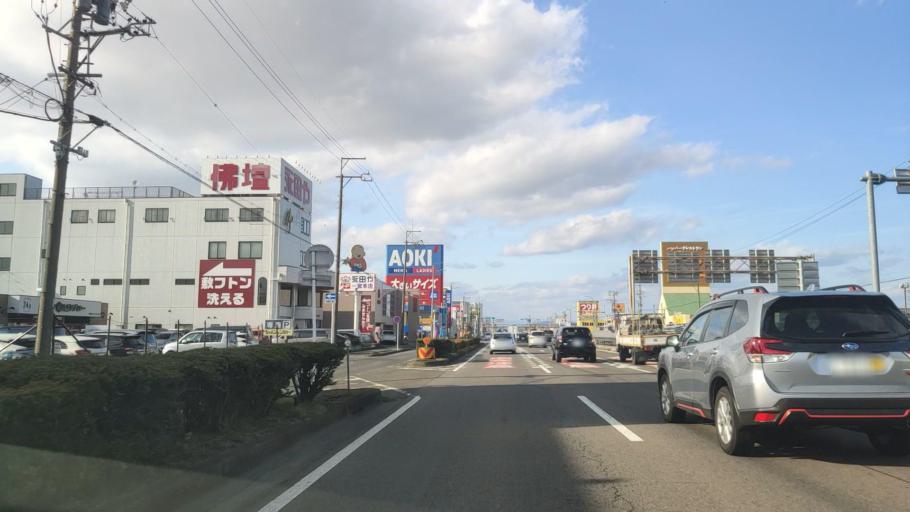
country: JP
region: Aichi
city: Ichinomiya
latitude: 35.3020
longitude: 136.8220
